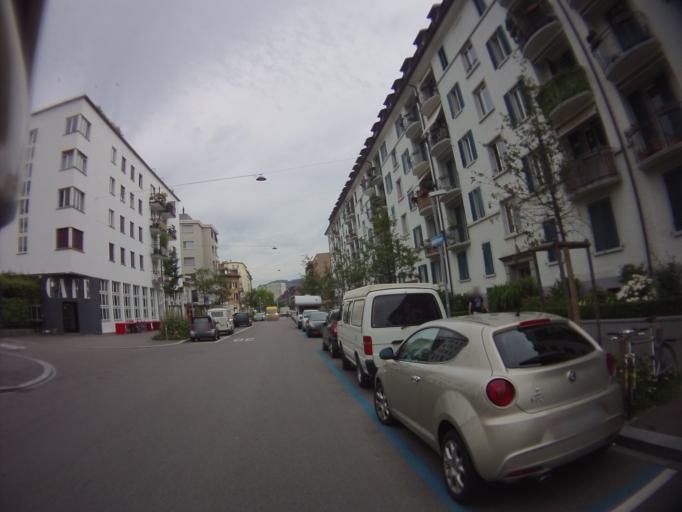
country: CH
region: Zurich
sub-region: Bezirk Zuerich
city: Aussersihl
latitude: 47.3775
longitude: 8.5163
